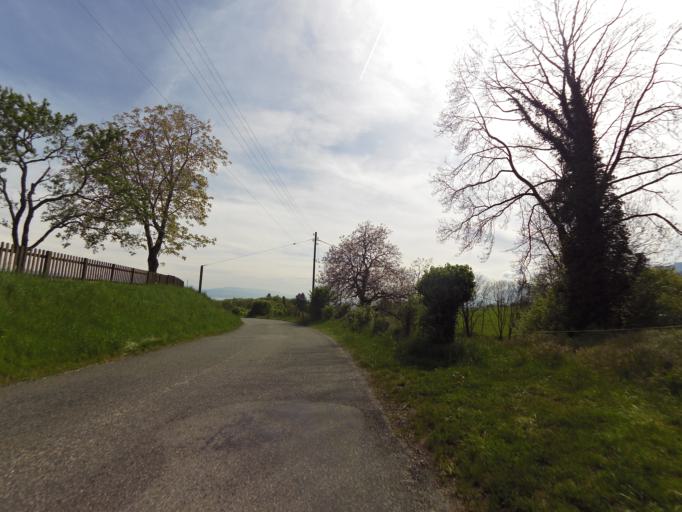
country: CH
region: Vaud
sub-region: Nyon District
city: Genolier
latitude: 46.4506
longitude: 6.2212
